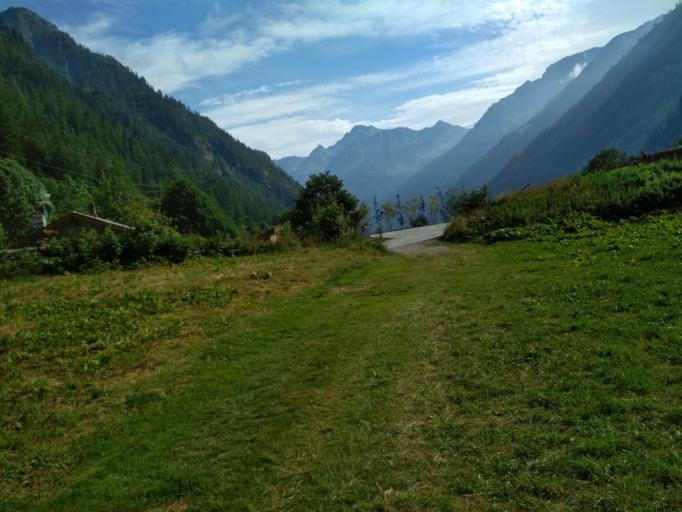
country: IT
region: Aosta Valley
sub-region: Valle d'Aosta
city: Gressoney-La-Trinite
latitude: 45.8091
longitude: 7.8264
